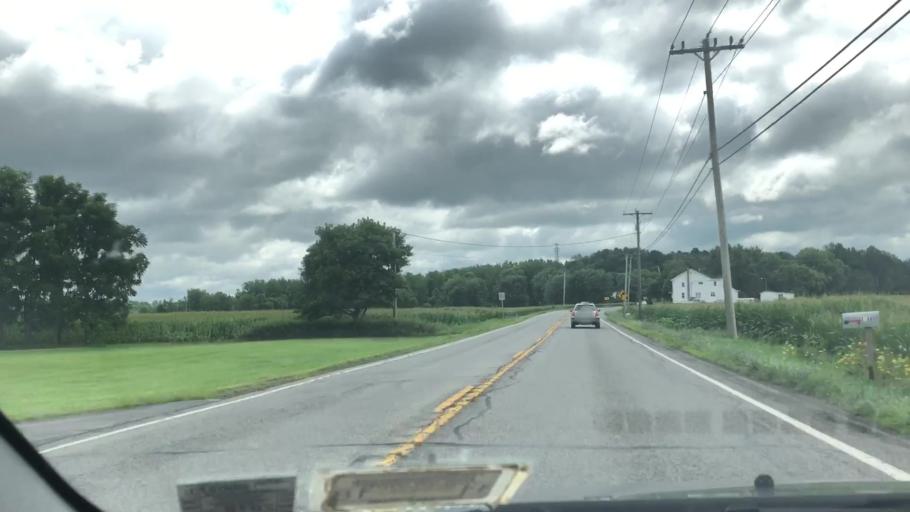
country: US
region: New York
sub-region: Wayne County
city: Macedon
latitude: 43.0990
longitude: -77.2941
